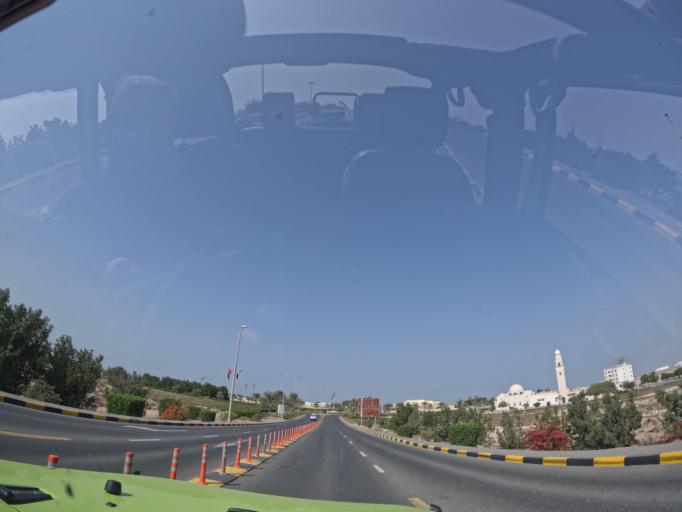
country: AE
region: Umm al Qaywayn
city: Umm al Qaywayn
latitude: 25.4781
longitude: 55.5239
